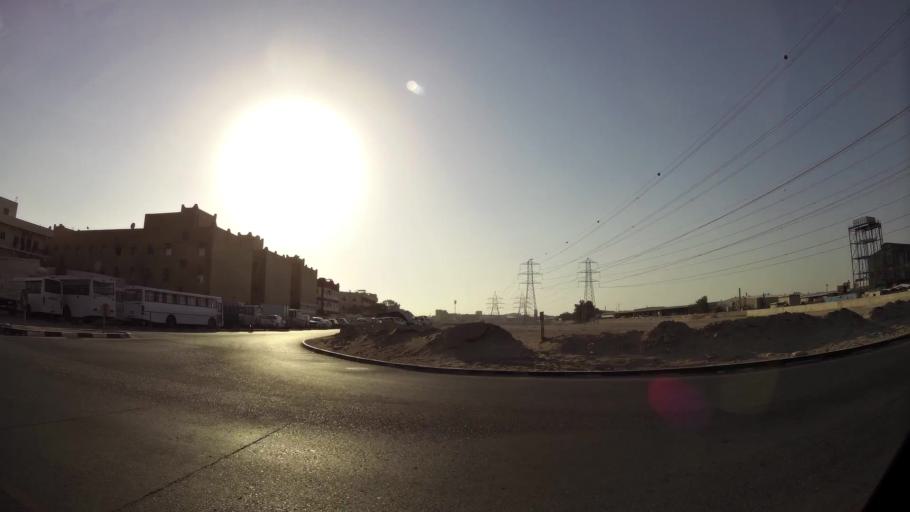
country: AE
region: Dubai
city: Dubai
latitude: 25.1339
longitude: 55.2416
